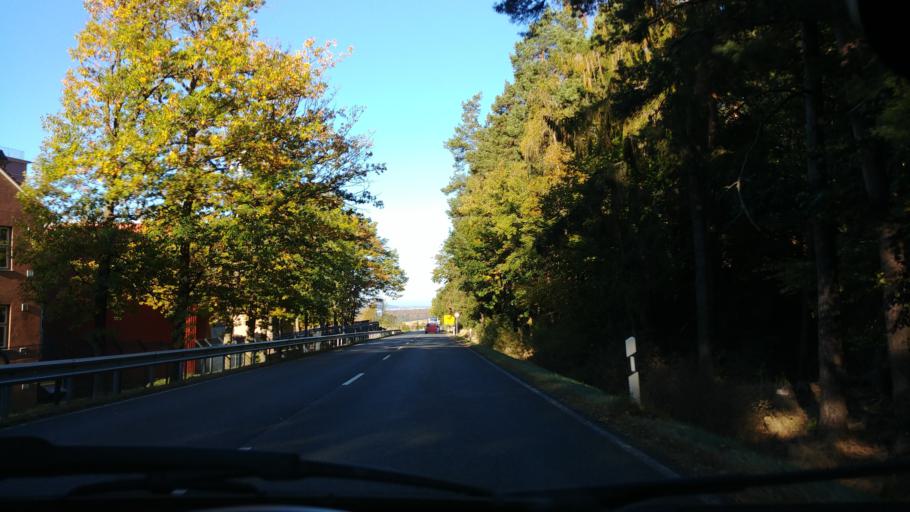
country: DE
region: Rheinland-Pfalz
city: Holzhausen an der Haide
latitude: 50.2108
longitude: 7.9231
